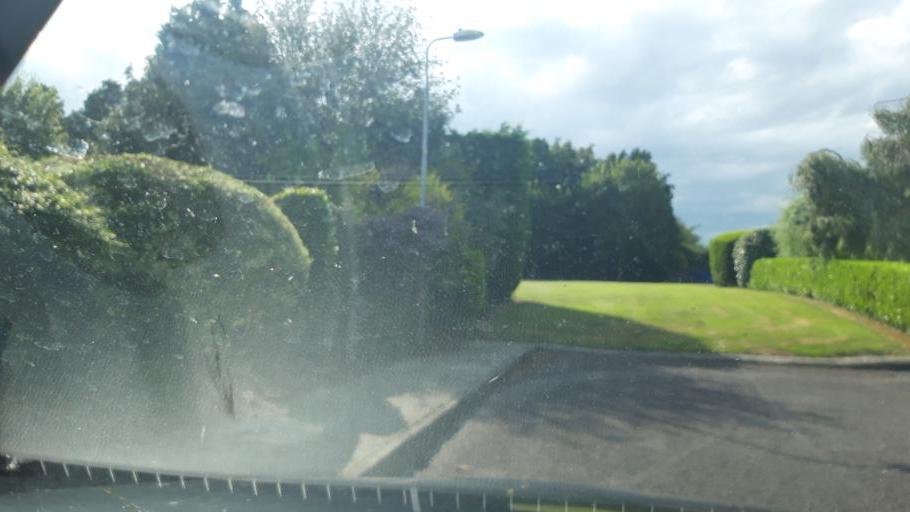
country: IE
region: Munster
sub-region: Waterford
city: Waterford
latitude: 52.2457
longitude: -7.0903
